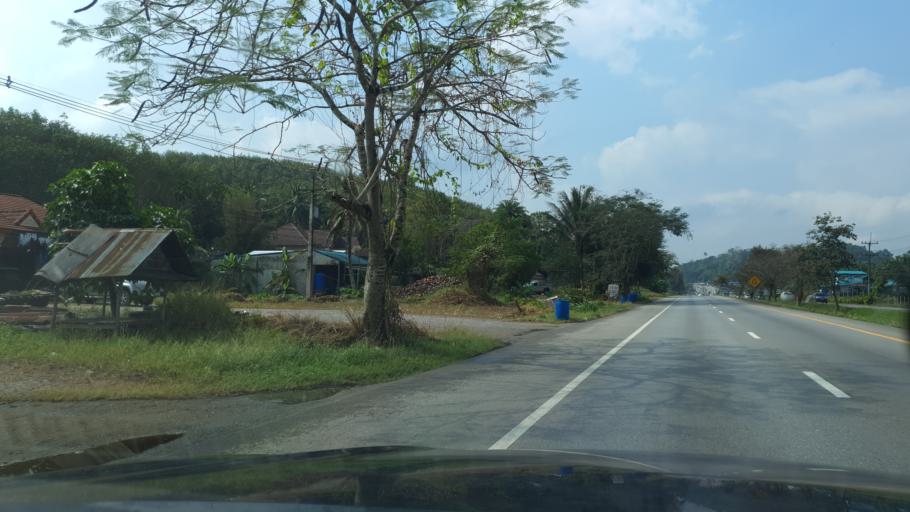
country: TH
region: Chumphon
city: Pathio
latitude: 10.8558
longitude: 99.2418
